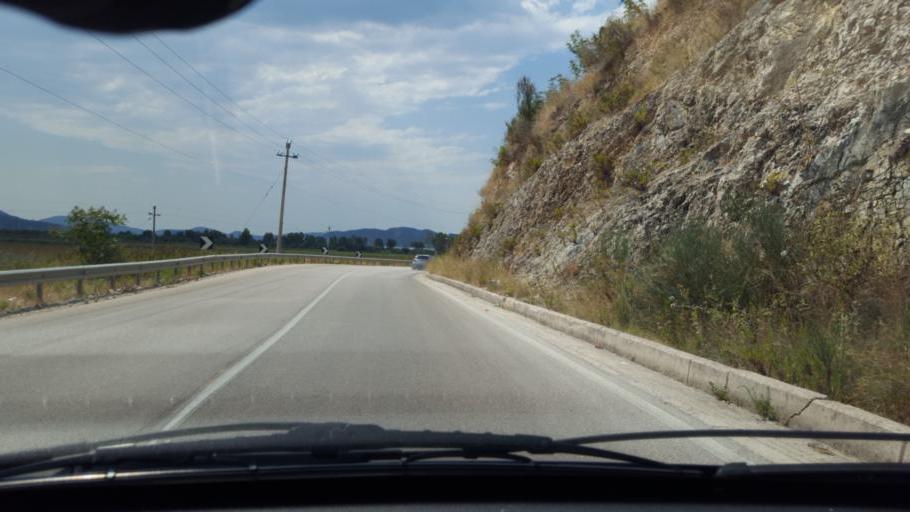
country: AL
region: Vlore
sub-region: Rrethi i Sarandes
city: Sarande
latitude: 39.8235
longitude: 20.0208
